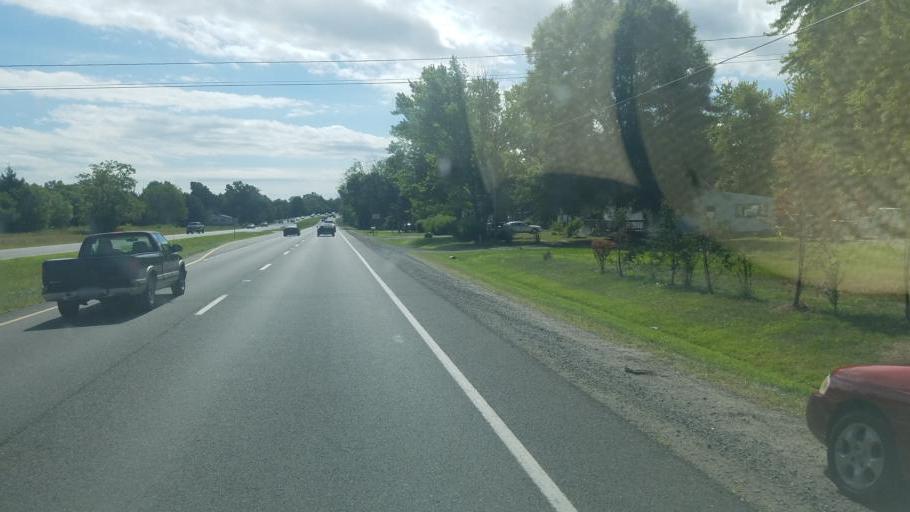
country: US
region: Virginia
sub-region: Fauquier County
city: Bealeton
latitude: 38.5619
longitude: -77.7463
